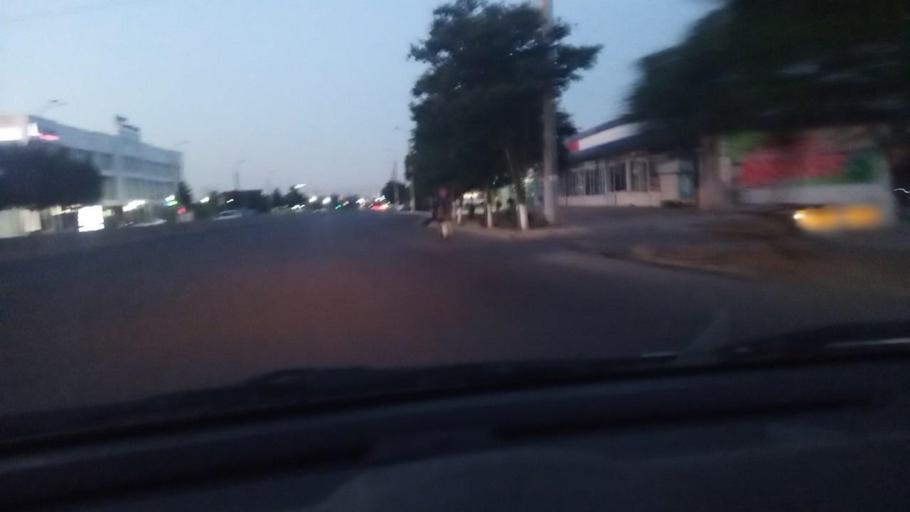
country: UZ
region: Toshkent Shahri
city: Tashkent
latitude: 41.2526
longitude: 69.2172
